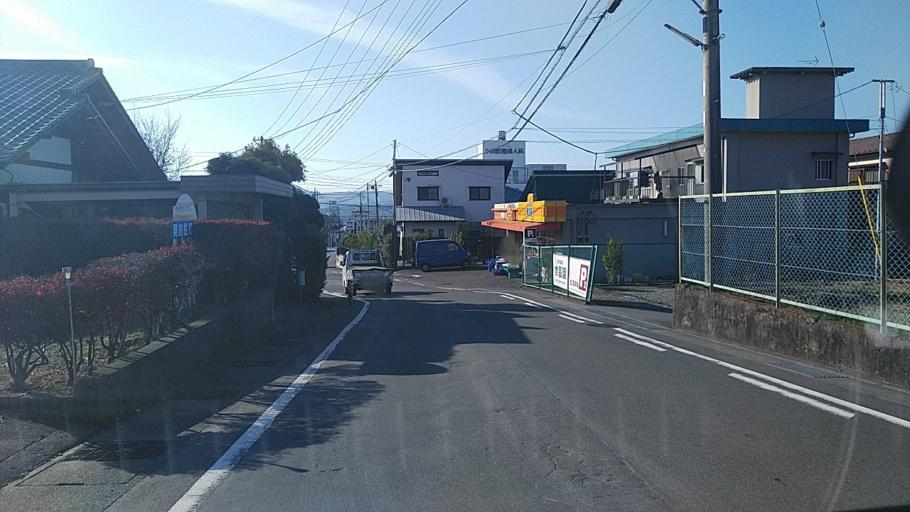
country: JP
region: Shizuoka
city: Fujinomiya
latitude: 35.2365
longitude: 138.6181
